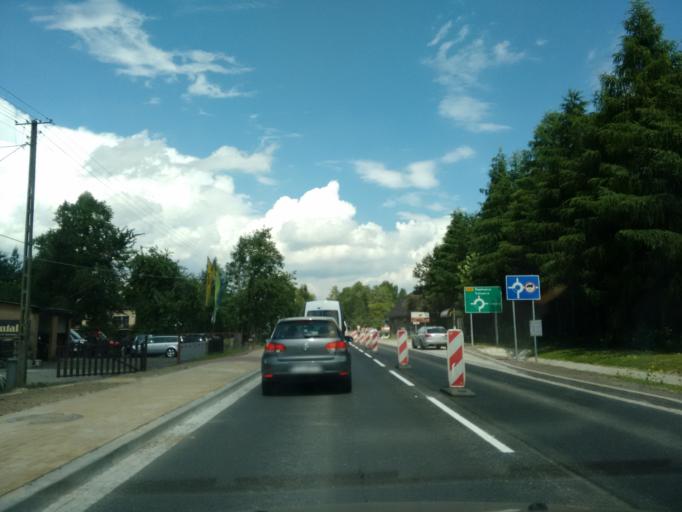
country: PL
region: Silesian Voivodeship
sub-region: Powiat cieszynski
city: Pruchna
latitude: 49.8642
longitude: 18.6813
